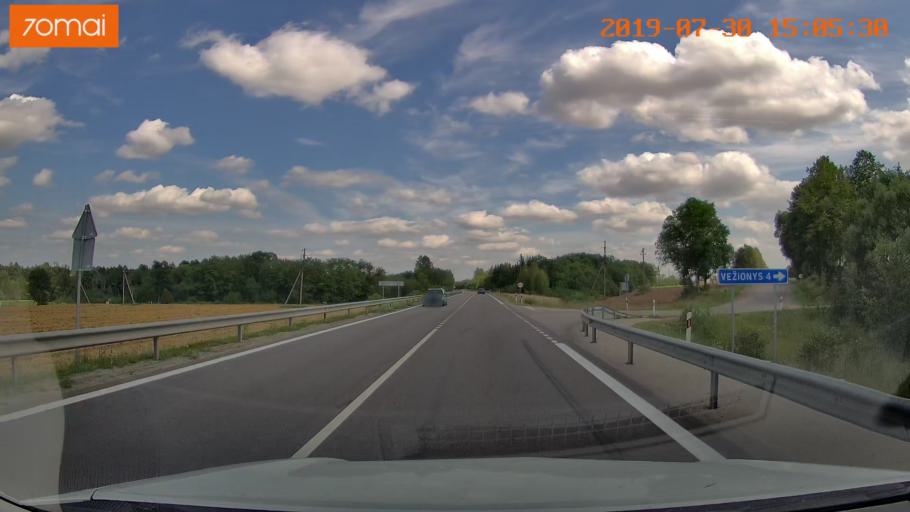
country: LT
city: Jieznas
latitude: 54.5769
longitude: 24.1162
